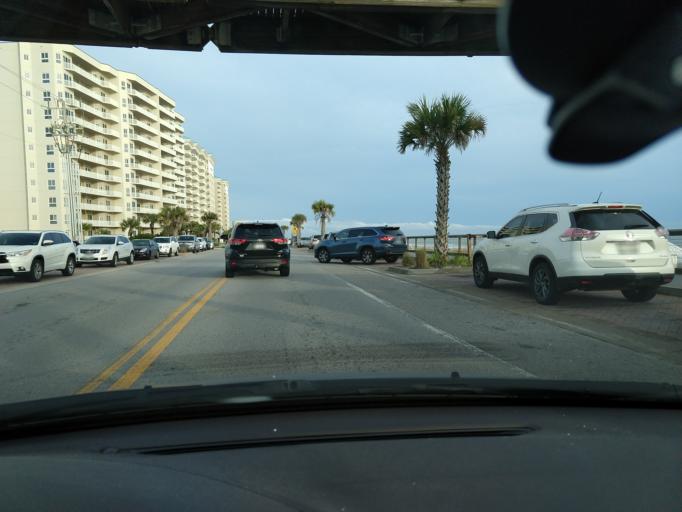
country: US
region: Florida
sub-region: Walton County
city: Miramar Beach
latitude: 30.3761
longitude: -86.3714
